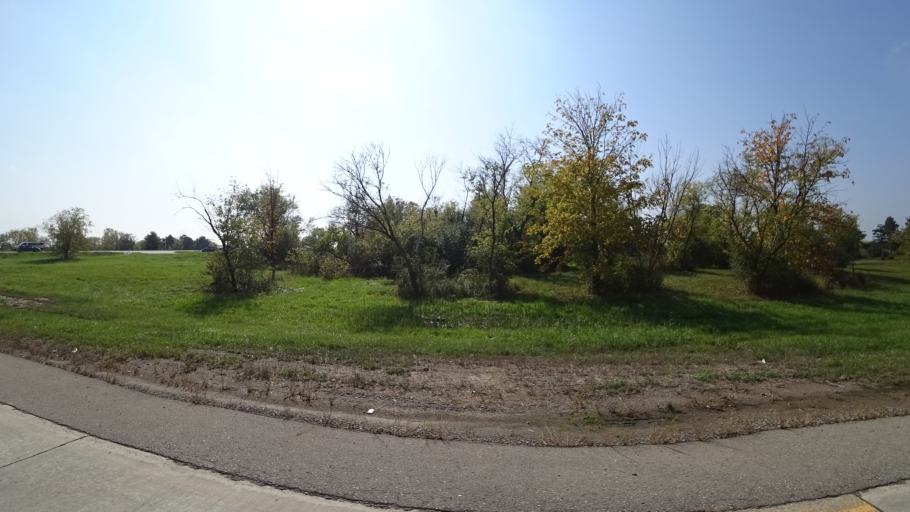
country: US
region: Michigan
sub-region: Washtenaw County
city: Ann Arbor
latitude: 42.2474
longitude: -83.7626
